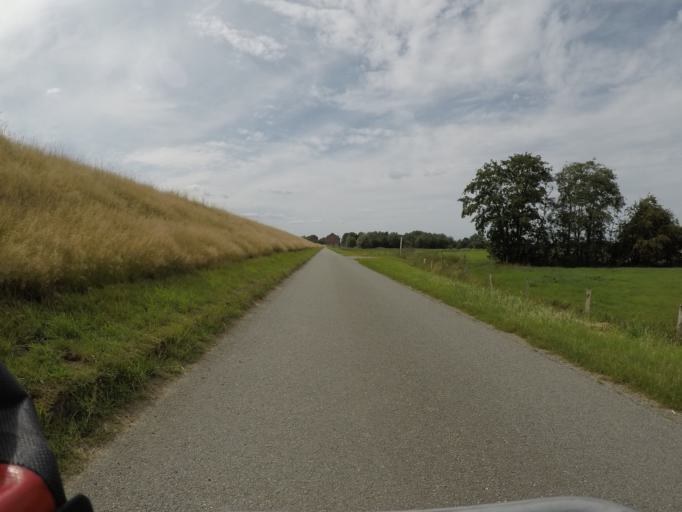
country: DE
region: Lower Saxony
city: Winsen
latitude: 53.3794
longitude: 10.2306
